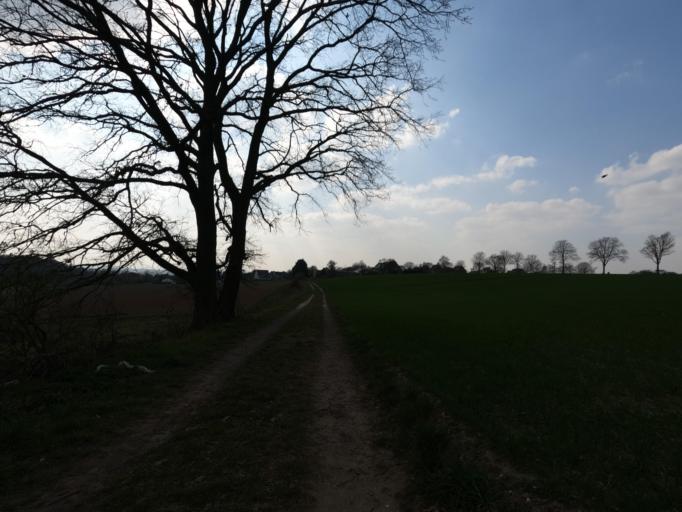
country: DE
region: North Rhine-Westphalia
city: Huckelhoven
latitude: 51.0634
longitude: 6.2338
